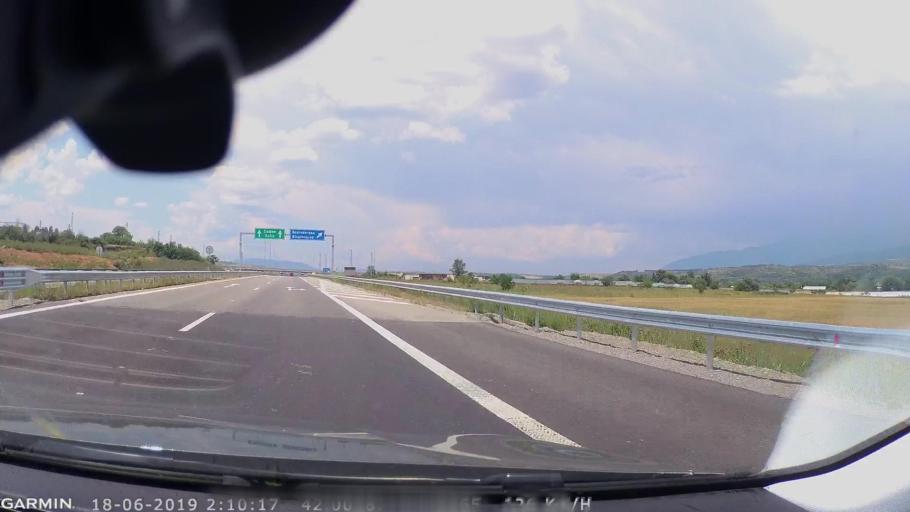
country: BG
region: Blagoevgrad
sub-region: Obshtina Blagoevgrad
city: Blagoevgrad
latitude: 41.9834
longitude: 23.0602
